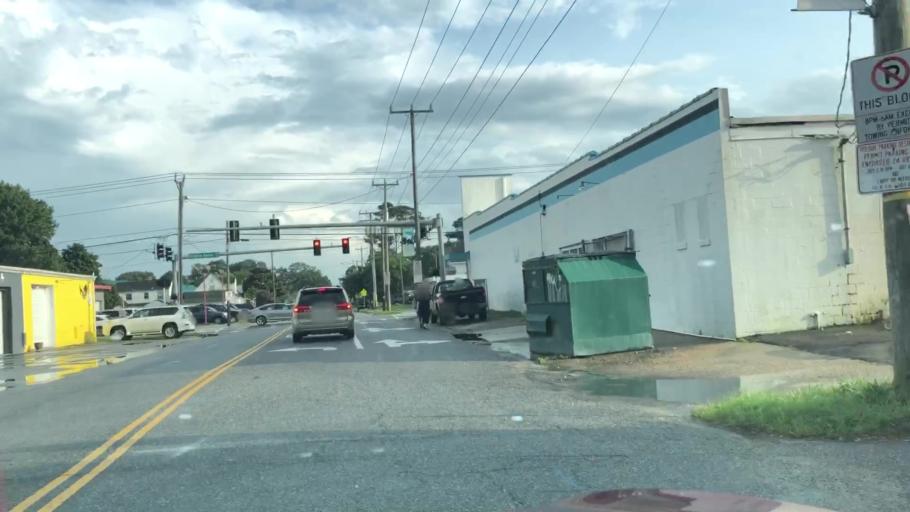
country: US
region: Virginia
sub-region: City of Virginia Beach
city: Virginia Beach
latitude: 36.8447
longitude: -75.9813
